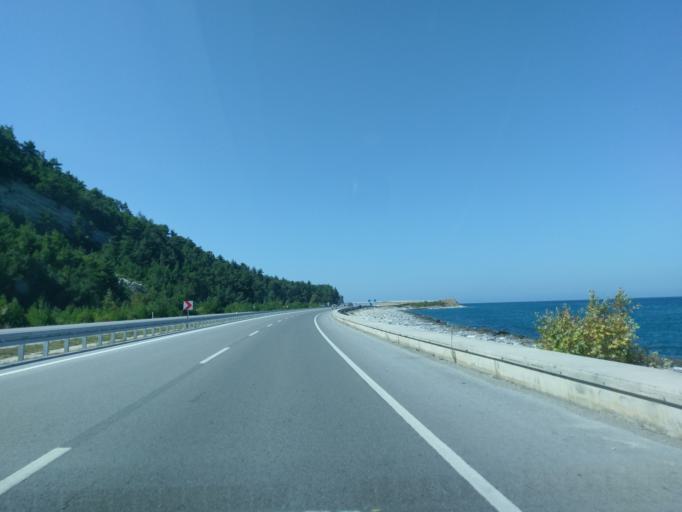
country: TR
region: Samsun
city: Yakakent
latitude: 41.6749
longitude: 35.4207
